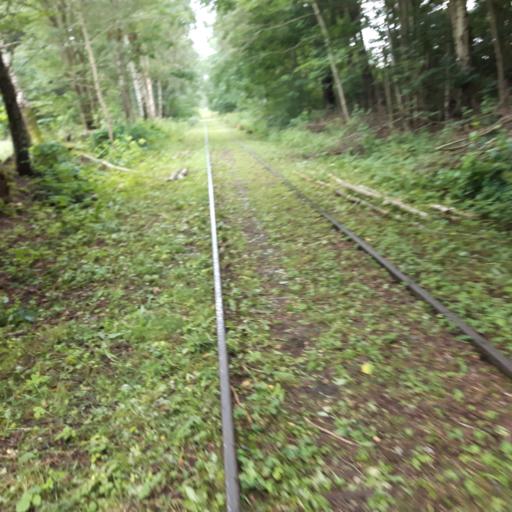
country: SE
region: Skane
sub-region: Ostra Goinge Kommun
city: Broby
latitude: 56.2627
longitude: 14.0719
